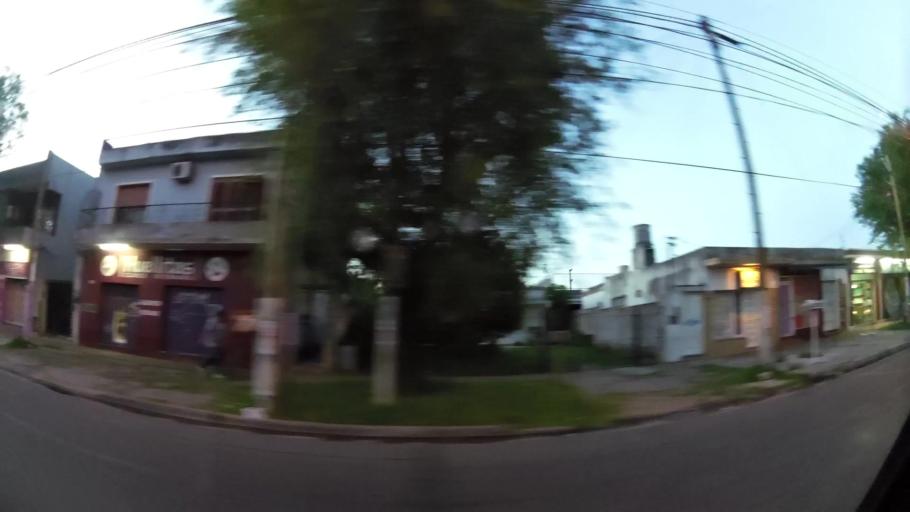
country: AR
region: Buenos Aires
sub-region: Partido de Quilmes
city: Quilmes
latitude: -34.7733
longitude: -58.2135
